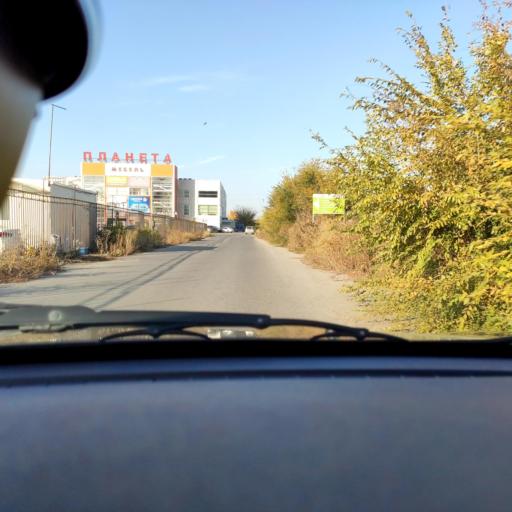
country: RU
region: Samara
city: Tol'yatti
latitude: 53.5509
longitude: 49.3251
